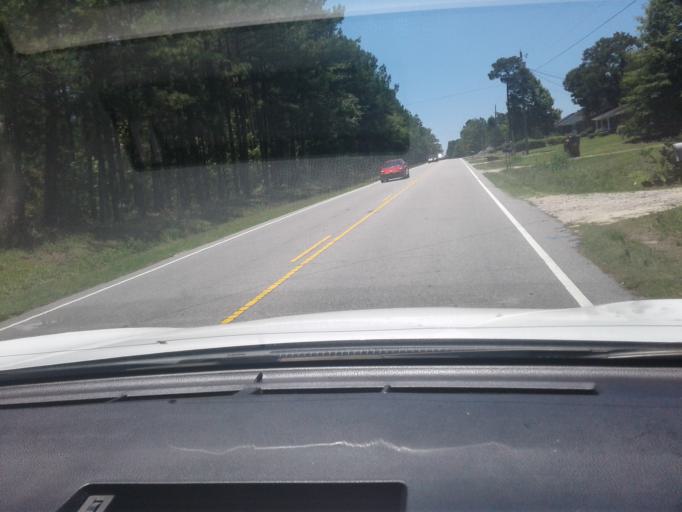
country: US
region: North Carolina
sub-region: Harnett County
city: Lillington
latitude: 35.3921
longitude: -78.8318
